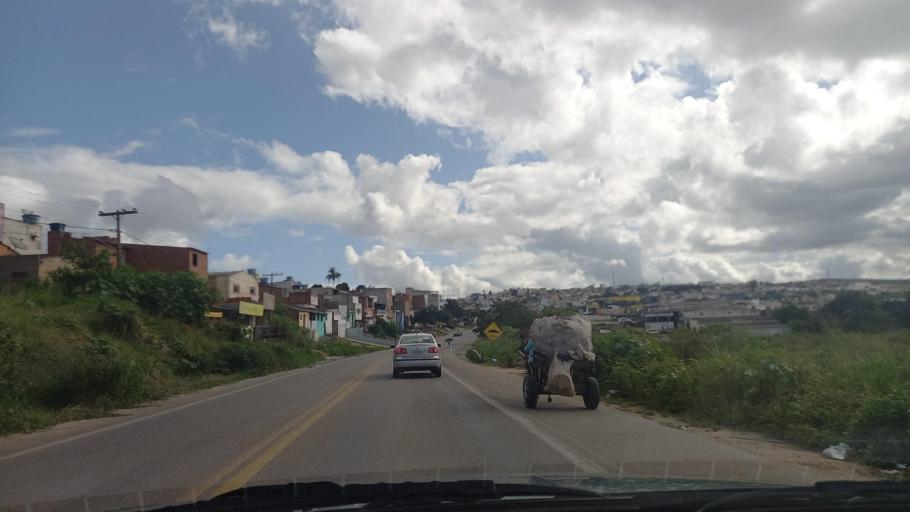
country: BR
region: Pernambuco
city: Garanhuns
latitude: -8.8788
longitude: -36.4826
